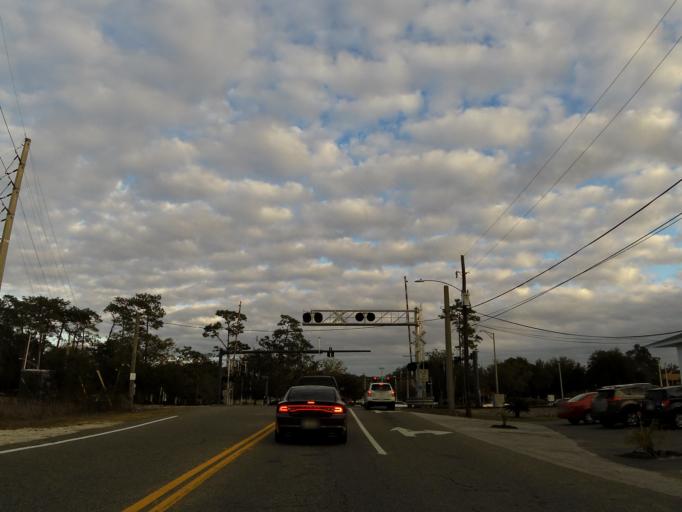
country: US
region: Florida
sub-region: Duval County
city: Jacksonville
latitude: 30.3030
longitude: -81.7204
